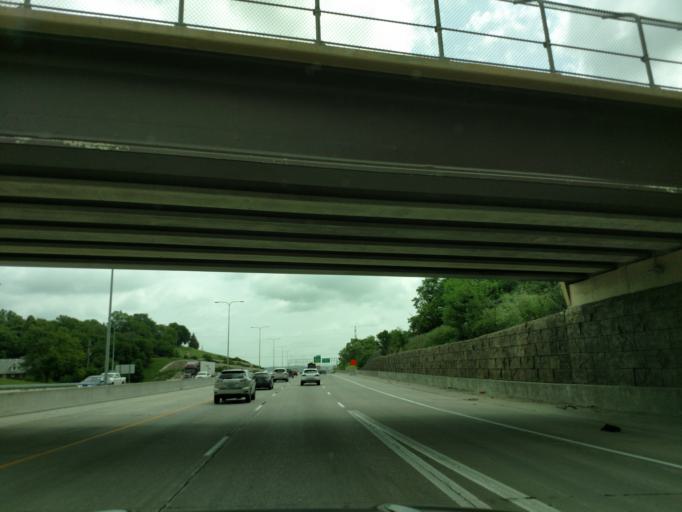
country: US
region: Nebraska
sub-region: Douglas County
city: Omaha
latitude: 41.2306
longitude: -95.9247
